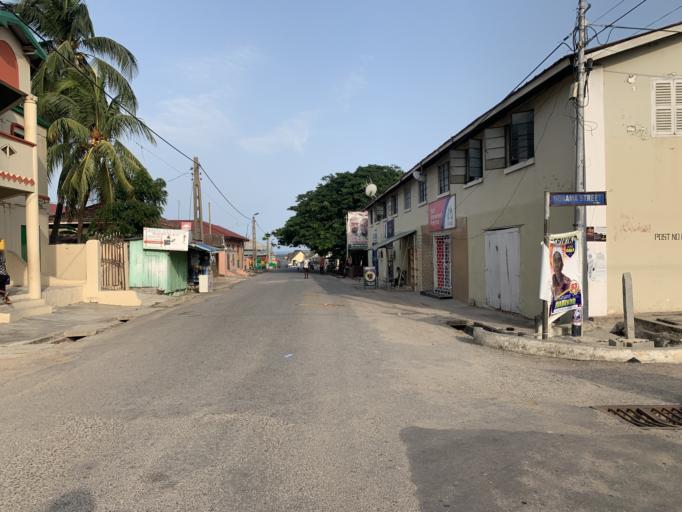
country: GH
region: Central
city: Winneba
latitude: 5.3387
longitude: -0.6215
